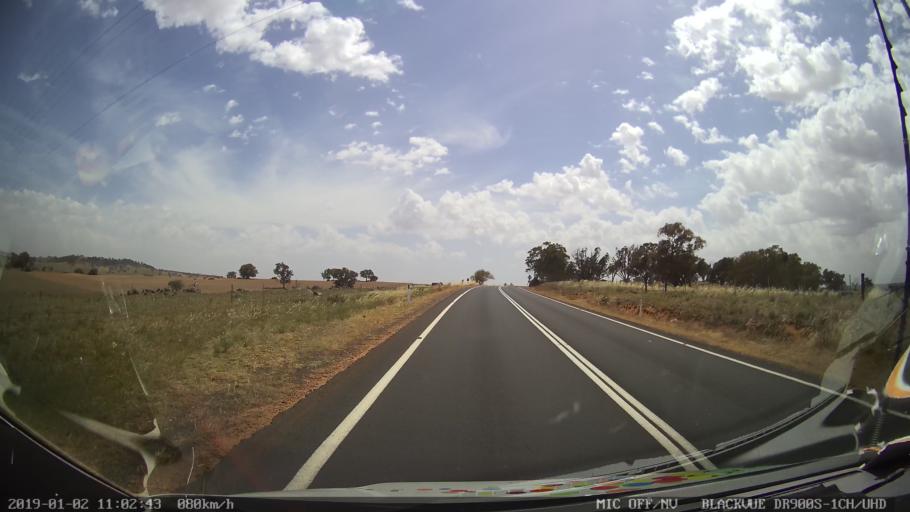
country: AU
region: New South Wales
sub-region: Young
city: Young
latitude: -34.5831
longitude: 148.3292
